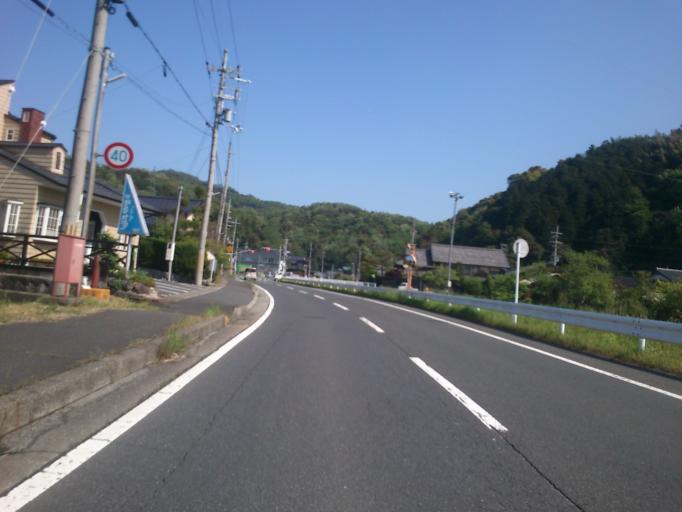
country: JP
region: Kyoto
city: Miyazu
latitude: 35.5731
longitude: 135.1611
